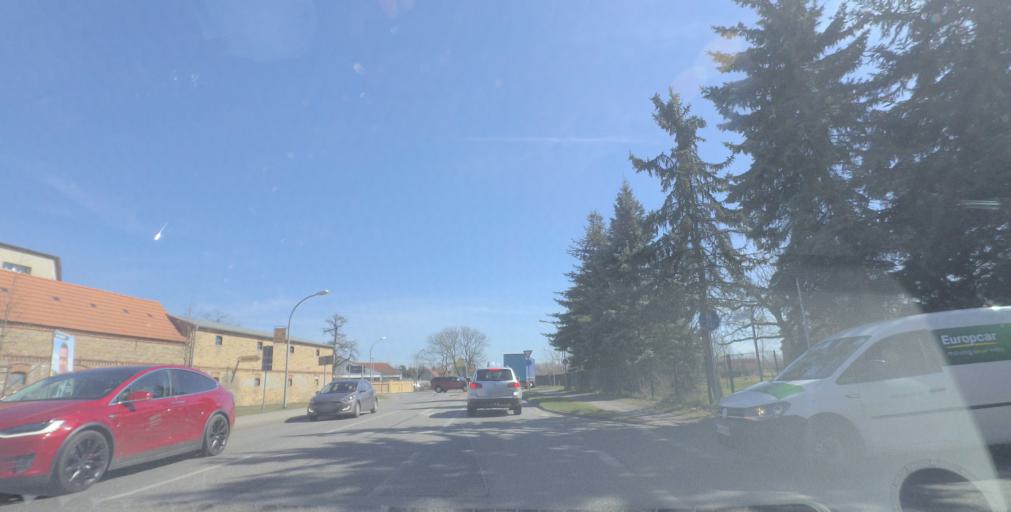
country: DE
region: Brandenburg
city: Neuruppin
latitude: 52.9458
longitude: 12.8483
